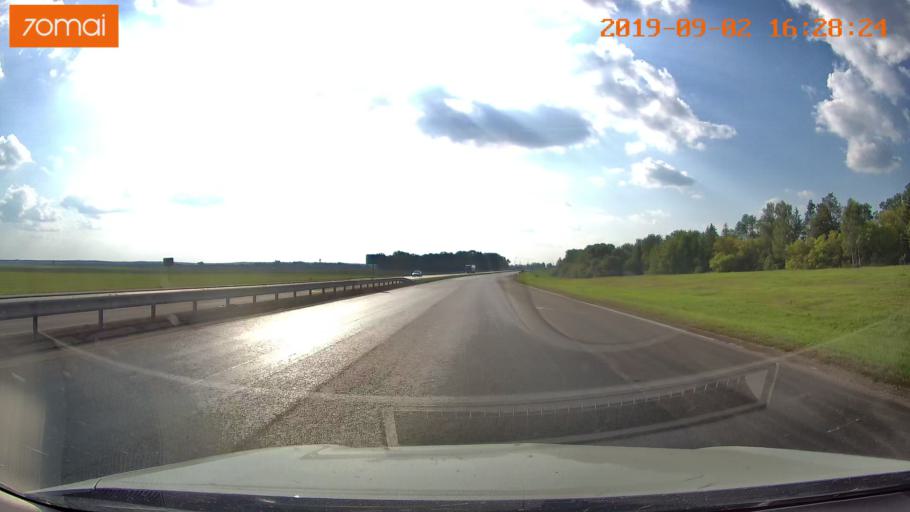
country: BY
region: Minsk
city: Smilavichy
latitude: 53.7635
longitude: 28.1780
